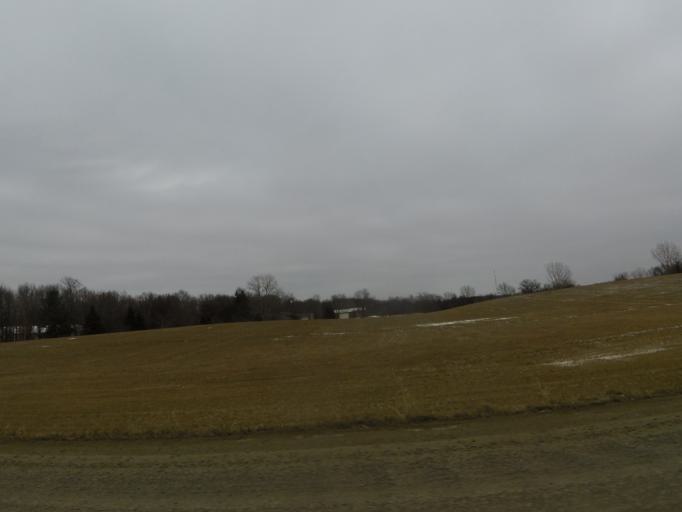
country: US
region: Minnesota
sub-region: Wright County
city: Montrose
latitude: 45.0568
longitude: -93.8592
